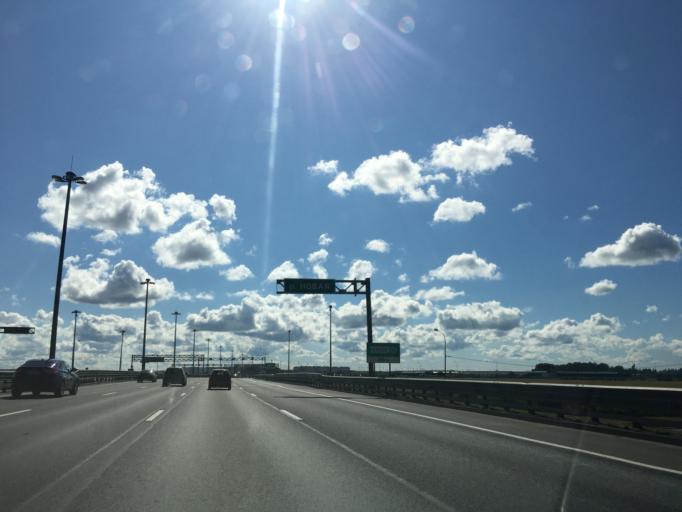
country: RU
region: St.-Petersburg
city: Uritsk
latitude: 59.8176
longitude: 30.2119
